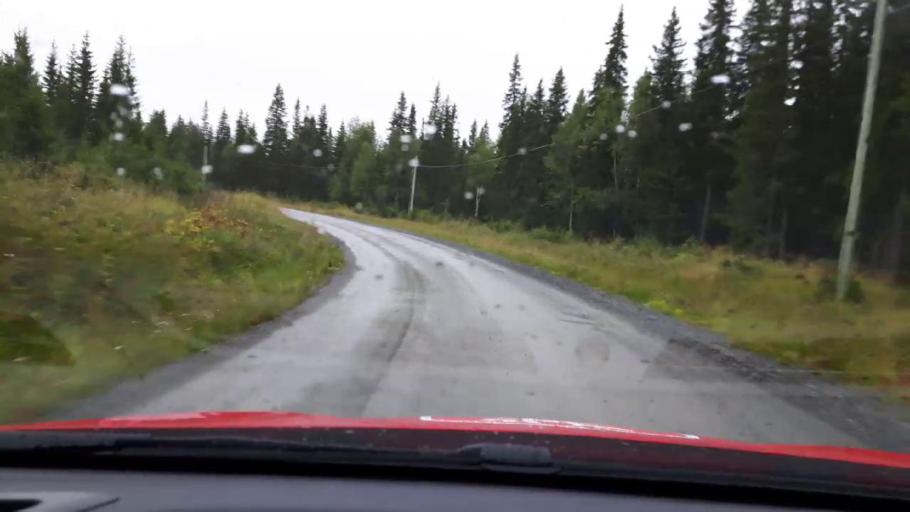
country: SE
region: Jaemtland
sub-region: Are Kommun
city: Are
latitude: 63.4459
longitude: 12.8039
